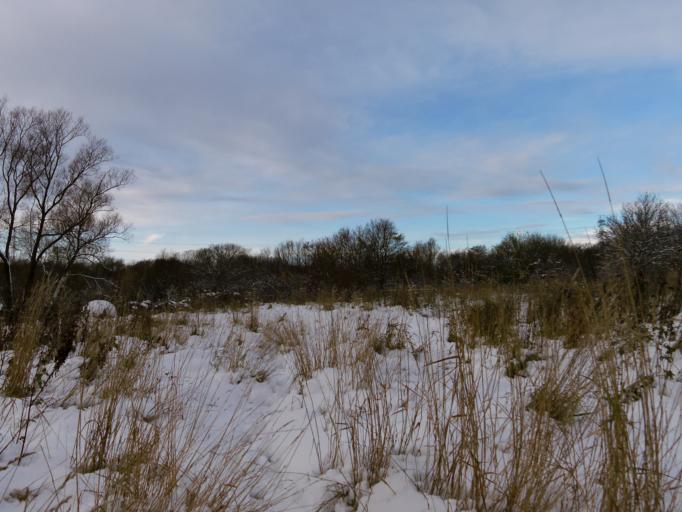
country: DK
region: Central Jutland
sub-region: Arhus Kommune
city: Stavtrup
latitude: 56.1280
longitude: 10.1382
